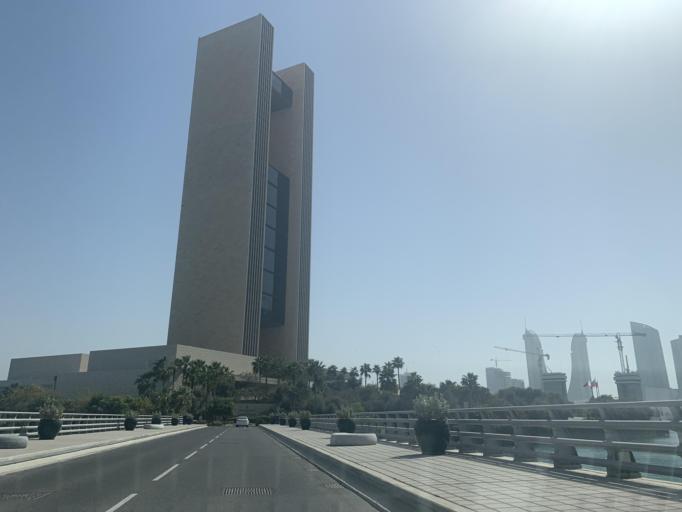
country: BH
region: Muharraq
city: Al Muharraq
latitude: 26.2495
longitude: 50.5818
